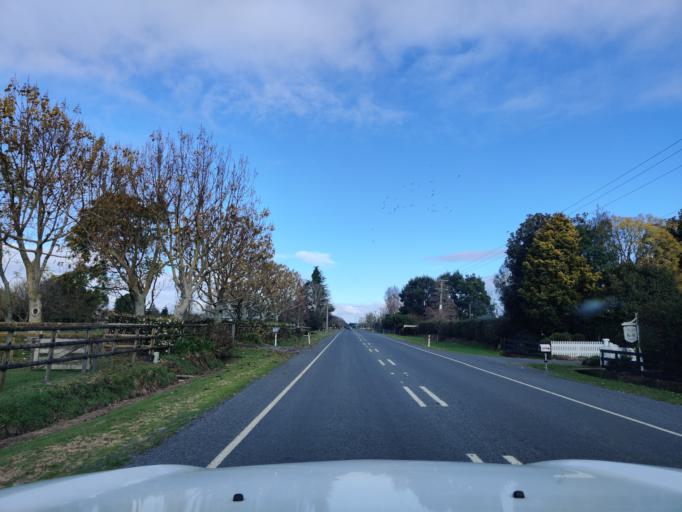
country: NZ
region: Waikato
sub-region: Waipa District
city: Cambridge
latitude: -37.8812
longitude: 175.4389
